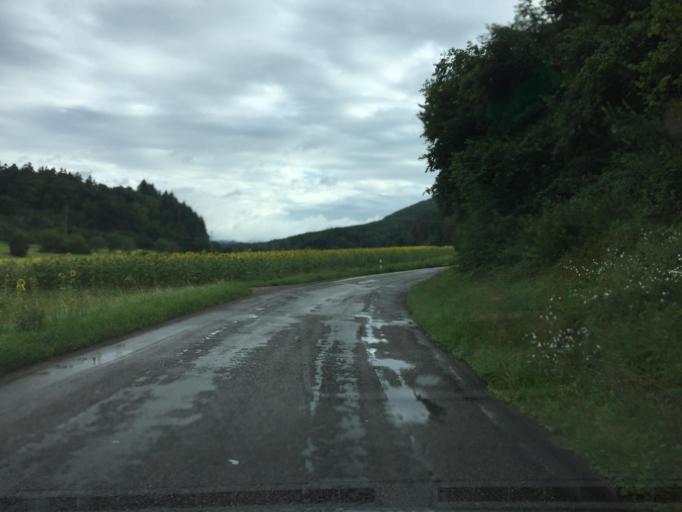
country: CH
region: Schaffhausen
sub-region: Bezirk Unterklettgau
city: Wilchingen
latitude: 47.6391
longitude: 8.4503
